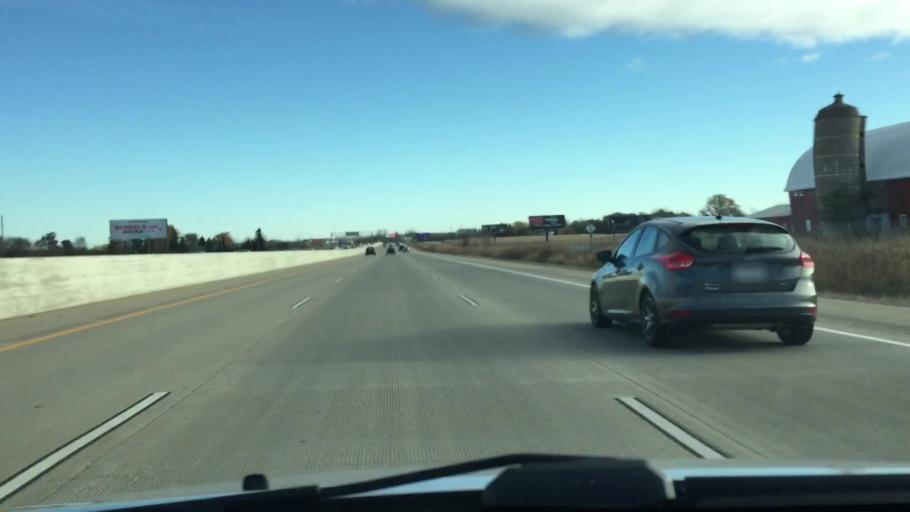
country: US
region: Wisconsin
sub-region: Winnebago County
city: Neenah
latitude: 44.1151
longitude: -88.5157
